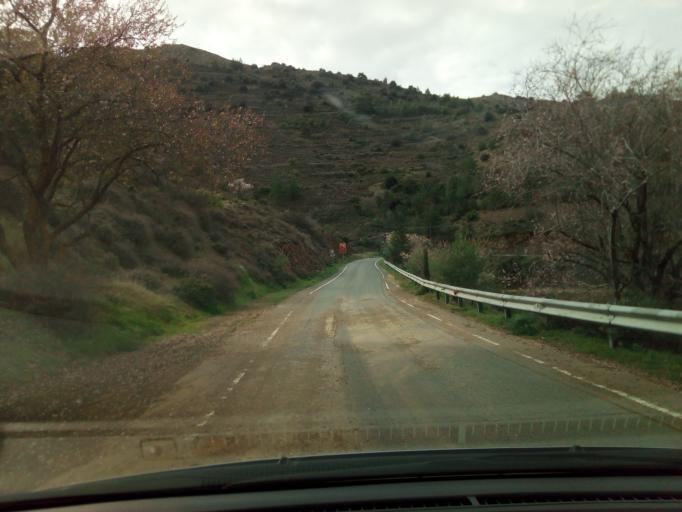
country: CY
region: Lefkosia
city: Klirou
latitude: 34.9586
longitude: 33.1705
